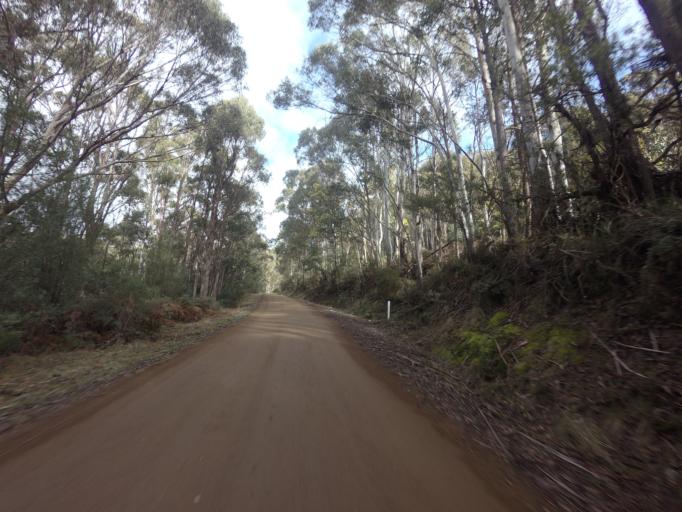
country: AU
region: Tasmania
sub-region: Derwent Valley
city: New Norfolk
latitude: -42.7887
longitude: 146.9346
